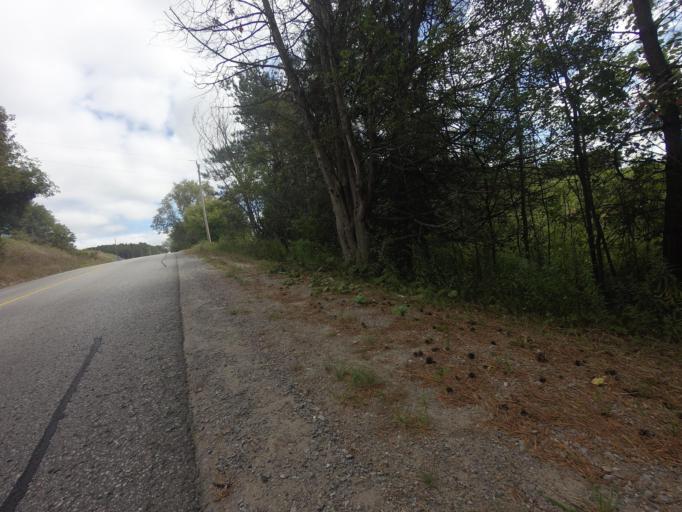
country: CA
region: Ontario
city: Uxbridge
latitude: 44.1114
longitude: -79.2303
